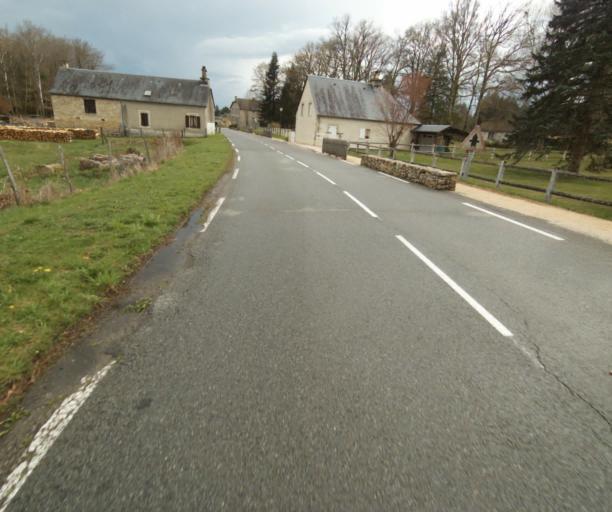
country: FR
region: Limousin
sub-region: Departement de la Correze
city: Saint-Privat
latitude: 45.2243
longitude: 2.0053
